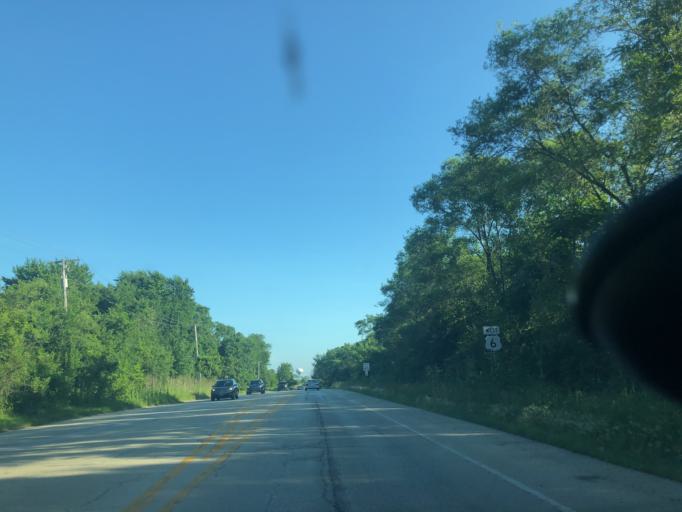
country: US
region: Illinois
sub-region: Cook County
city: Orland Hills
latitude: 41.5857
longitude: -87.8911
